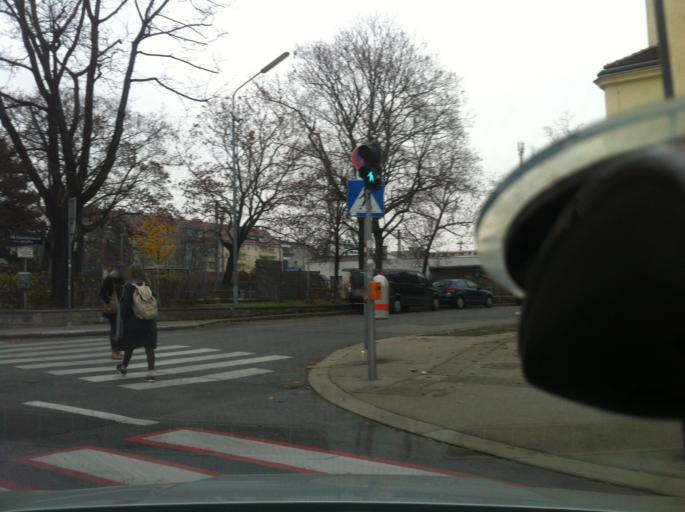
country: AT
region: Vienna
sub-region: Wien Stadt
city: Vienna
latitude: 48.1920
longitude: 16.3018
